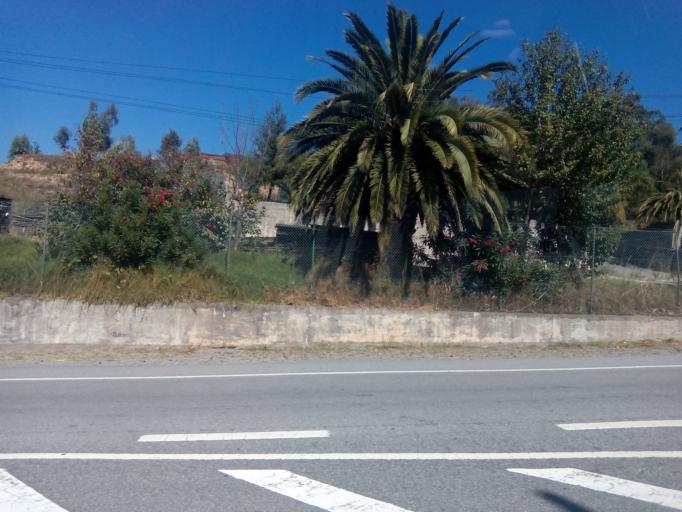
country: PT
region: Porto
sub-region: Paredes
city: Gandra
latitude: 41.1929
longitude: -8.4153
